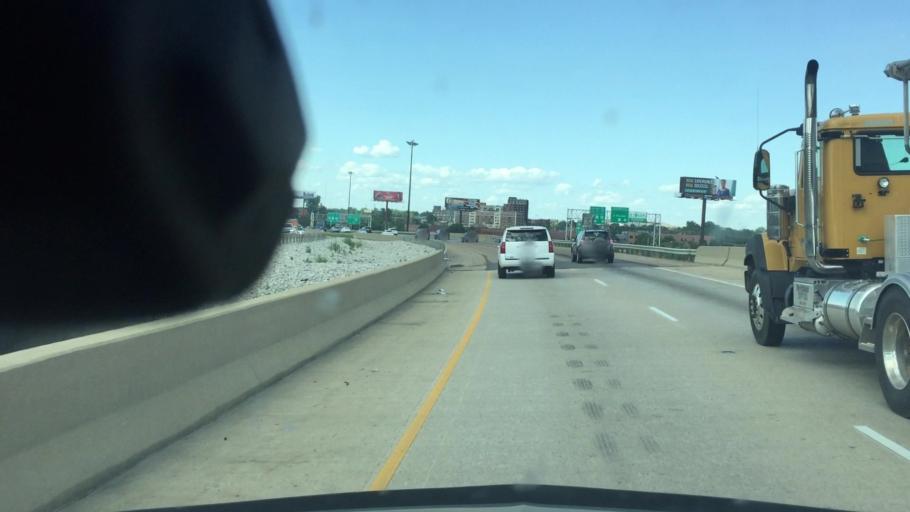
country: US
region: Illinois
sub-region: Saint Clair County
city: East Saint Louis
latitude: 38.6175
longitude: -90.1669
